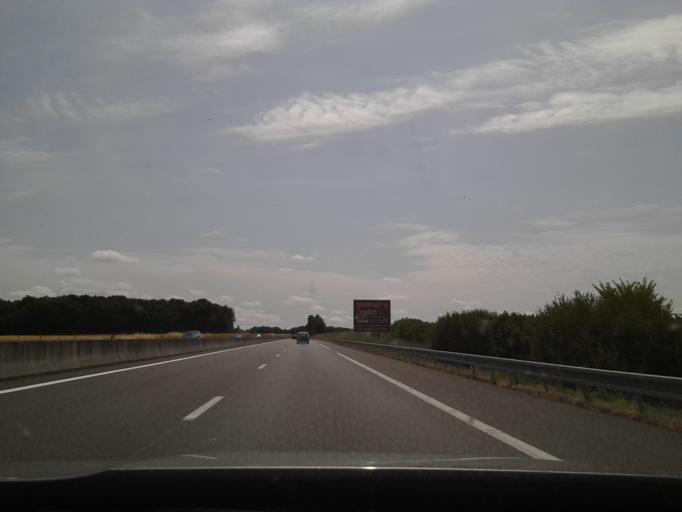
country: FR
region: Centre
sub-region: Departement d'Indre-et-Loire
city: Neuille-Pont-Pierre
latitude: 47.5921
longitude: 0.5491
